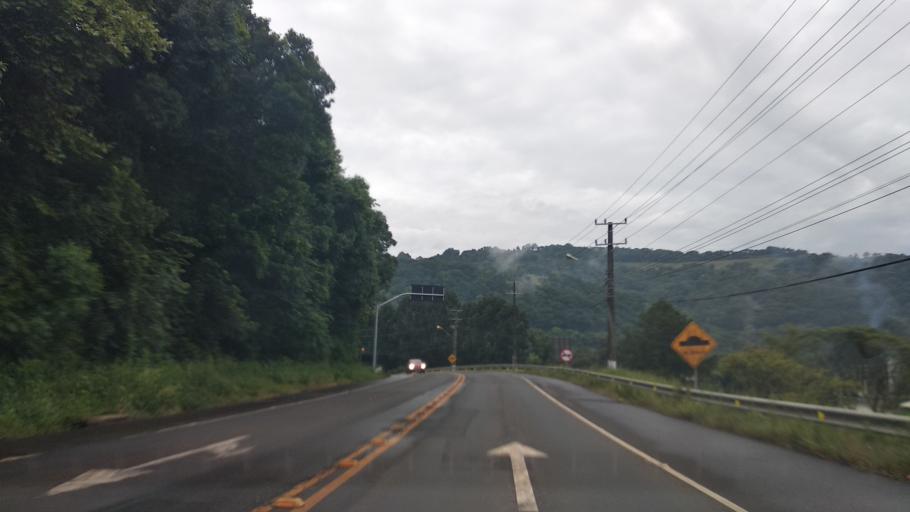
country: BR
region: Santa Catarina
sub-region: Videira
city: Videira
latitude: -27.0560
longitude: -51.2284
